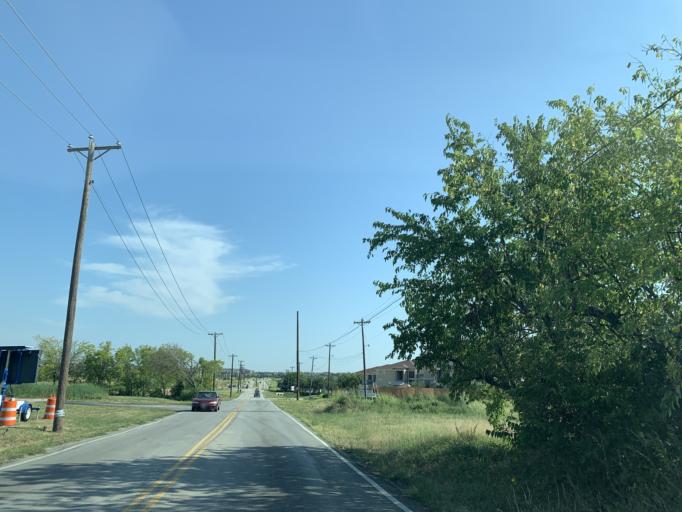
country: US
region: Texas
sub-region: Tarrant County
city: Blue Mound
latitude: 32.8997
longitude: -97.3069
